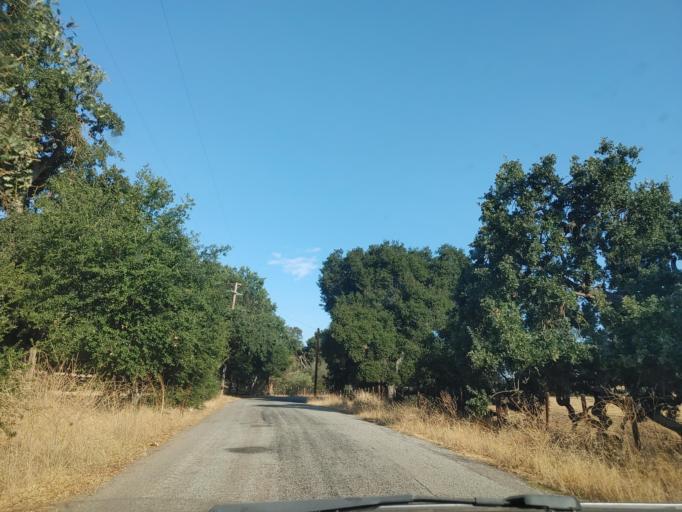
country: US
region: California
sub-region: San Benito County
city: Ridgemark
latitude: 36.7901
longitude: -121.2588
